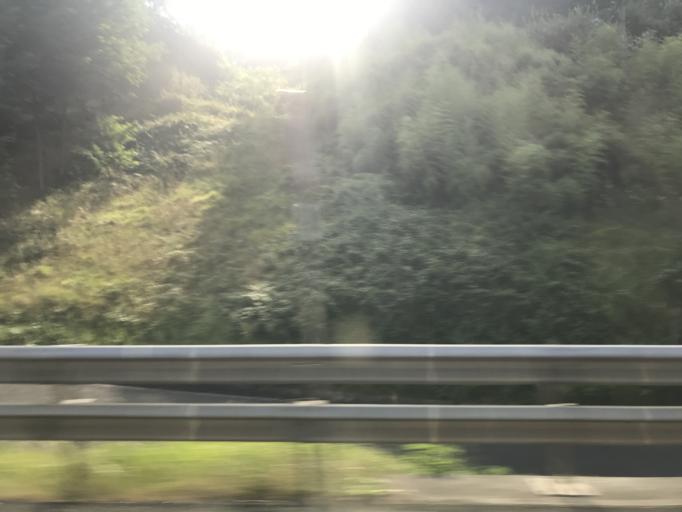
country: ES
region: Basque Country
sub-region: Provincia de Guipuzcoa
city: Villabona
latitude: 43.1903
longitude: -2.0509
